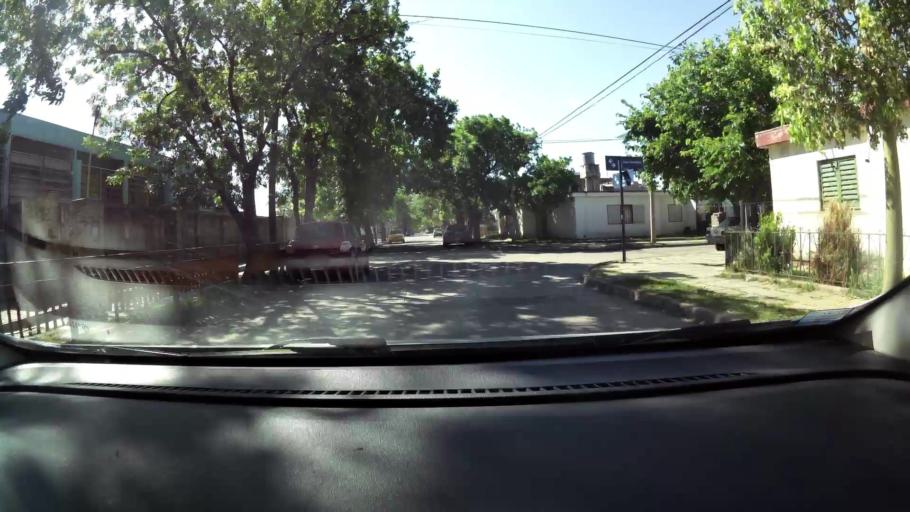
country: AR
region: Cordoba
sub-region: Departamento de Capital
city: Cordoba
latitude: -31.3636
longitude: -64.1675
